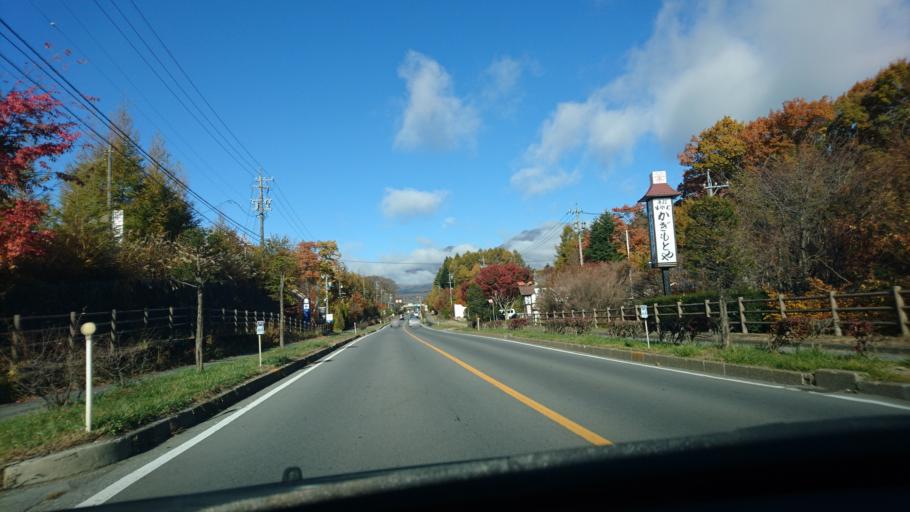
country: JP
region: Nagano
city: Saku
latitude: 36.3320
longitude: 138.6065
